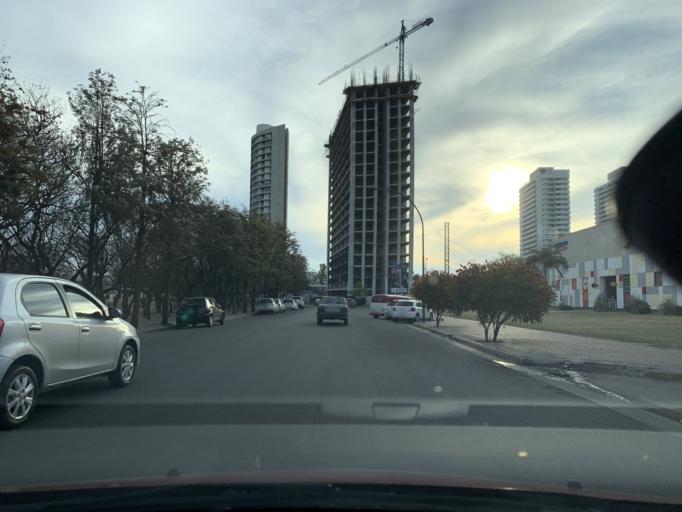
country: AR
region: Cordoba
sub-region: Departamento de Capital
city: Cordoba
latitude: -31.4092
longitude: -64.1708
